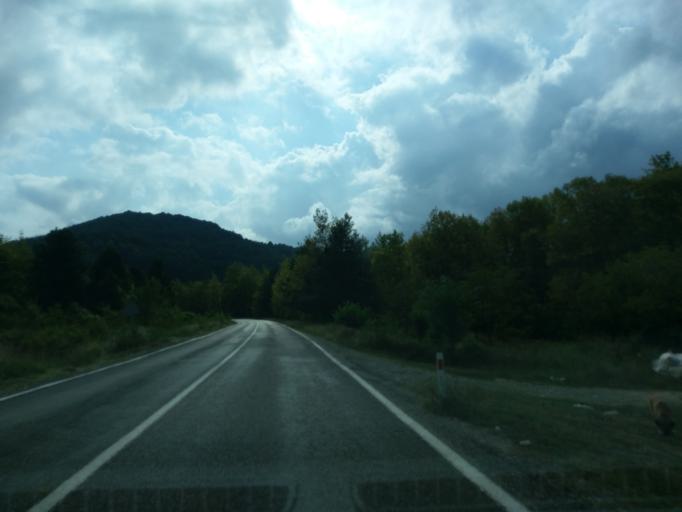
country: TR
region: Sinop
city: Yenikonak
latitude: 41.9399
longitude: 34.7207
